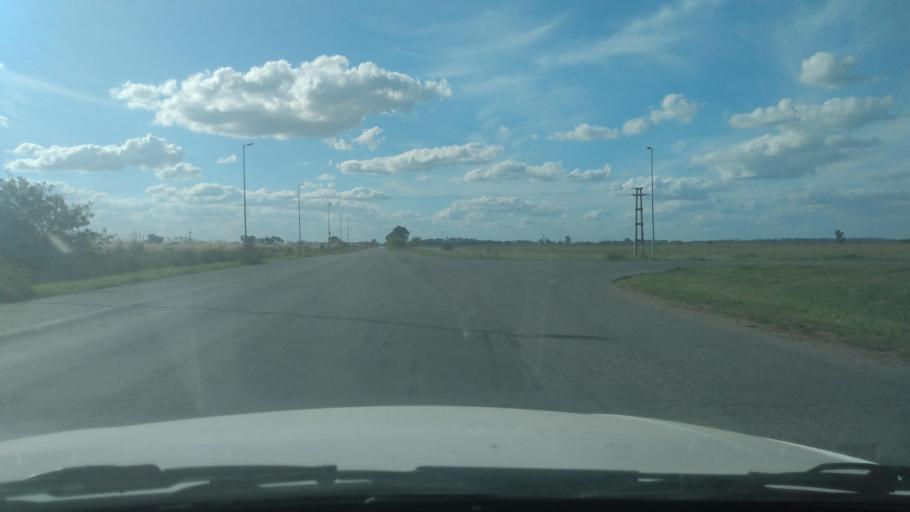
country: AR
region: Buenos Aires
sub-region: Partido de Navarro
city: Navarro
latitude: -34.9865
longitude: -59.3154
